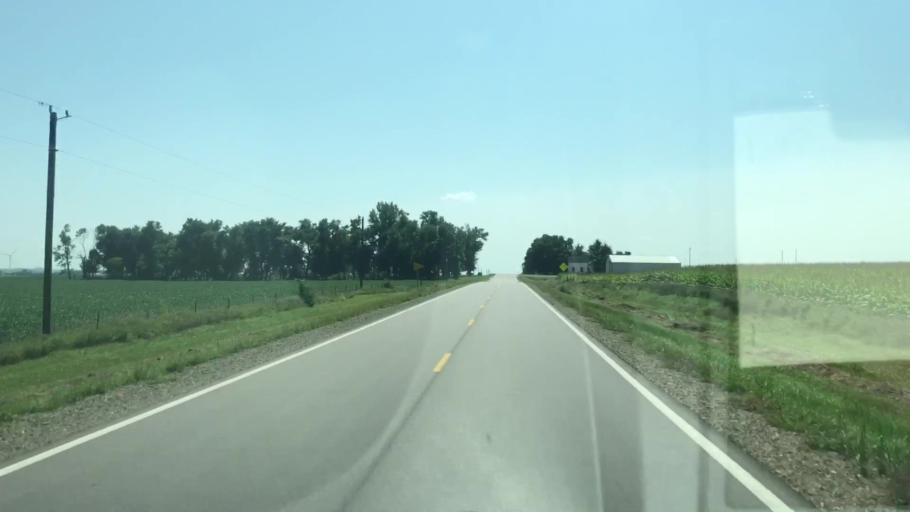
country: US
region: Iowa
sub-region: O'Brien County
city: Sanborn
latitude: 43.2646
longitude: -95.7237
